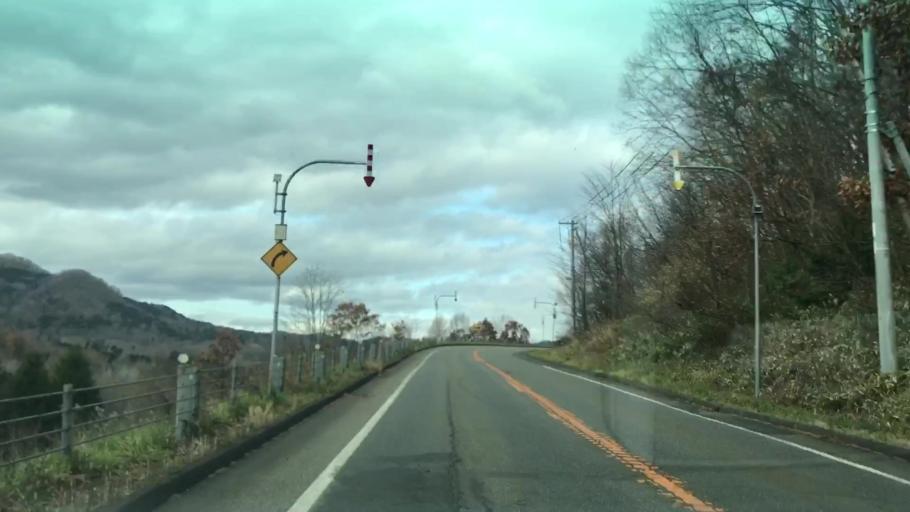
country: JP
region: Hokkaido
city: Shimo-furano
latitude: 42.8850
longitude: 142.4337
